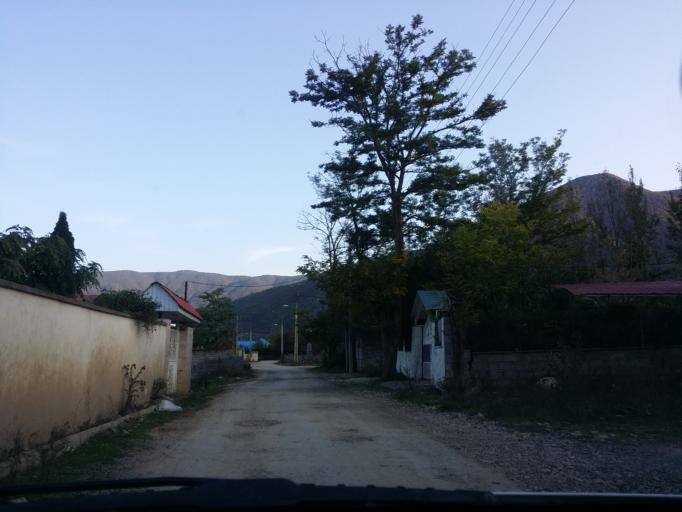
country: IR
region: Mazandaran
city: `Abbasabad
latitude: 36.5113
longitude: 51.1837
